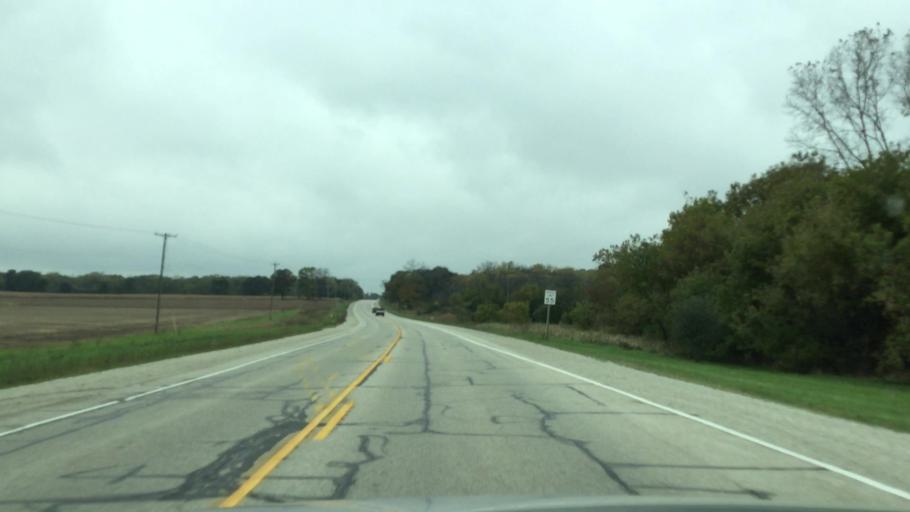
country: US
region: Wisconsin
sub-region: Racine County
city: Eagle Lake
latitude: 42.7427
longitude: -88.1464
